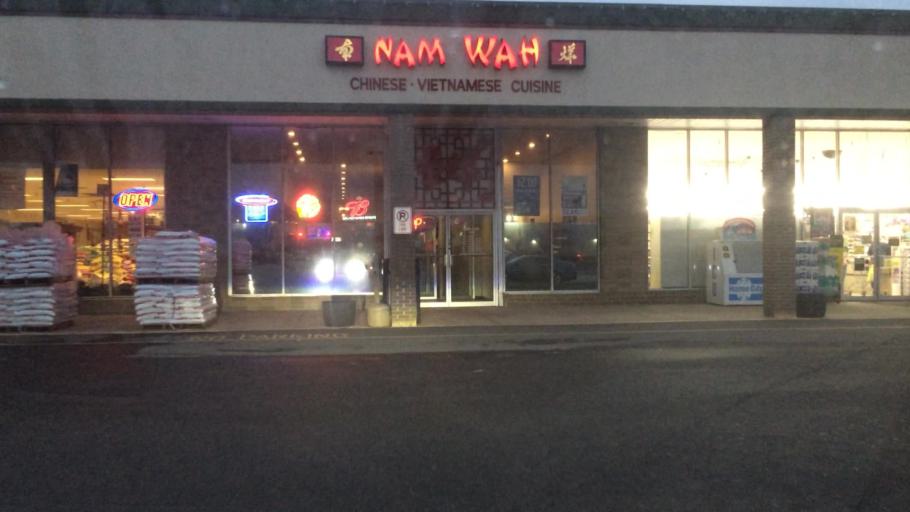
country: US
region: Ohio
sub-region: Cuyahoga County
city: Berea
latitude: 41.3734
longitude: -81.8672
